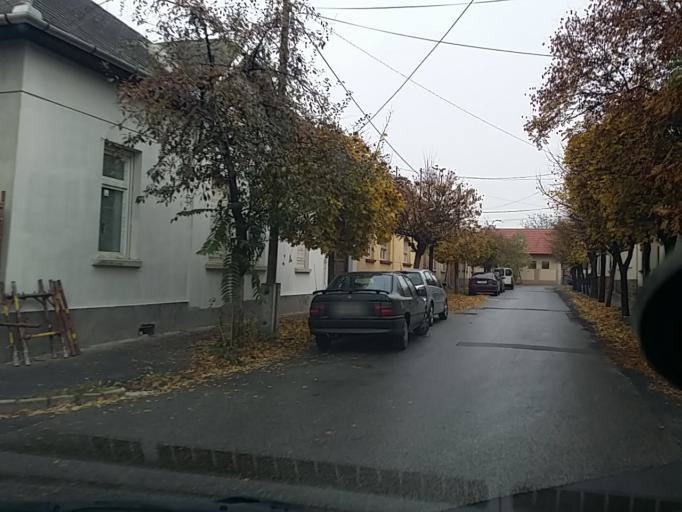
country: HU
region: Heves
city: Gyongyos
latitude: 47.7870
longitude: 19.9280
